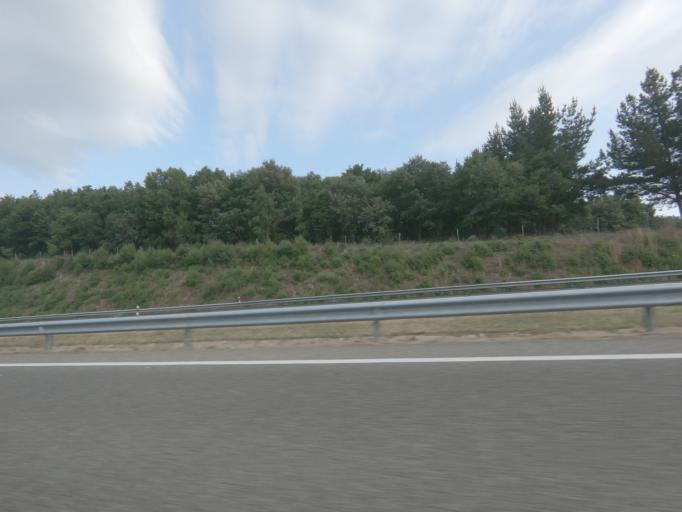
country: ES
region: Galicia
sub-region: Provincia de Ourense
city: Allariz
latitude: 42.2028
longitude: -7.7953
